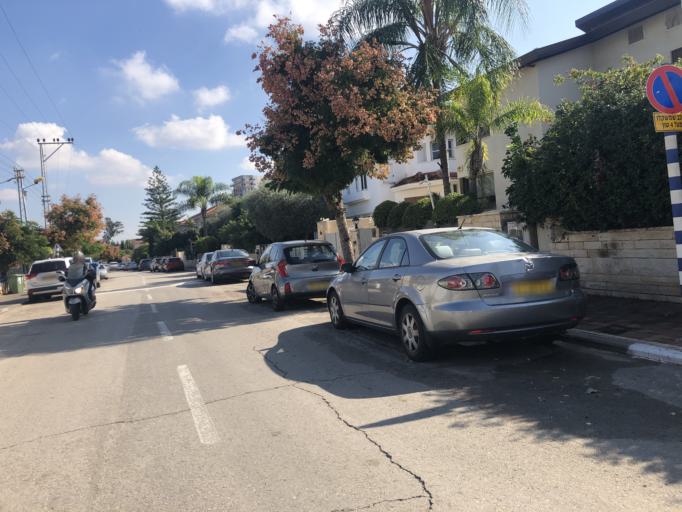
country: IL
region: Tel Aviv
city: Or Yehuda
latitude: 32.0291
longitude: 34.8700
